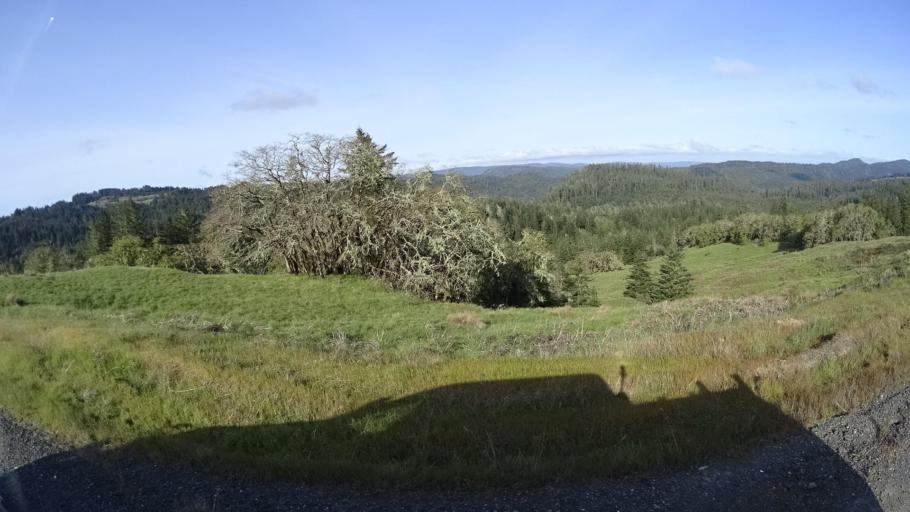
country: US
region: California
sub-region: Humboldt County
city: Hydesville
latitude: 40.6593
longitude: -123.9270
